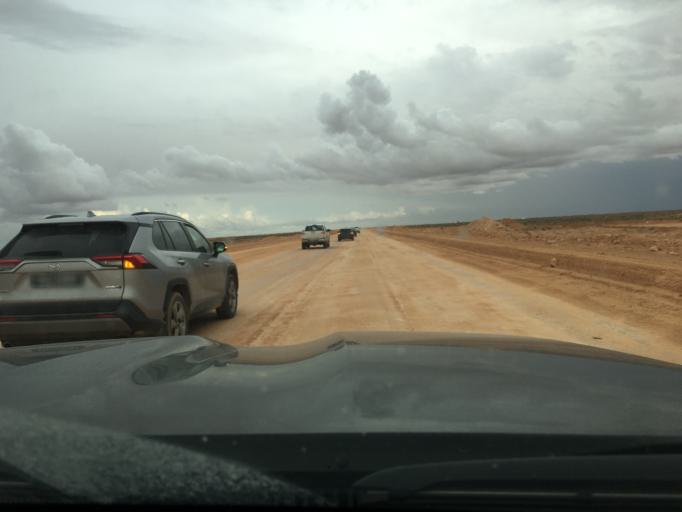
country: TN
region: Madanin
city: Medenine
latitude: 33.2738
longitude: 10.5894
